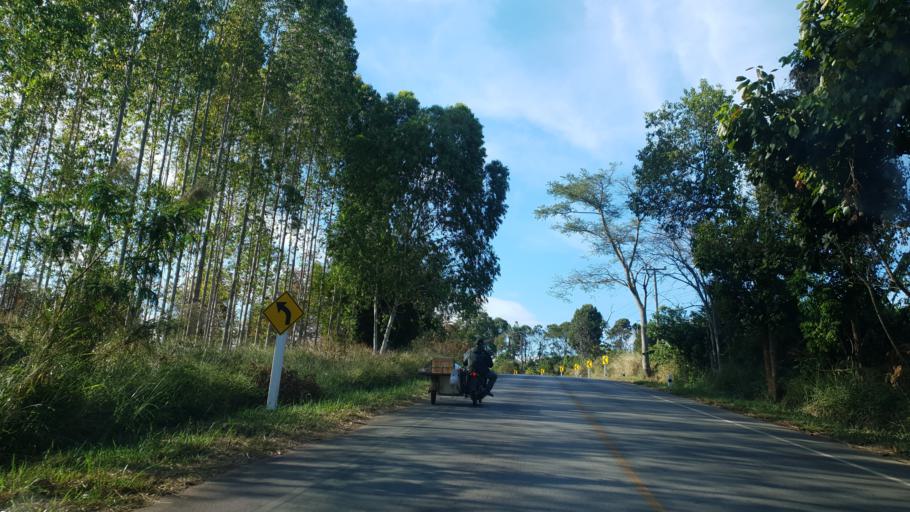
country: TH
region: Loei
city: Phu Ruea
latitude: 17.4448
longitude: 101.4994
